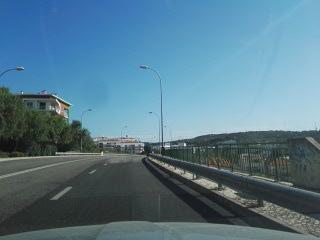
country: PT
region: Lisbon
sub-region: Oeiras
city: Alges
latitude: 38.7202
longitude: -9.2214
